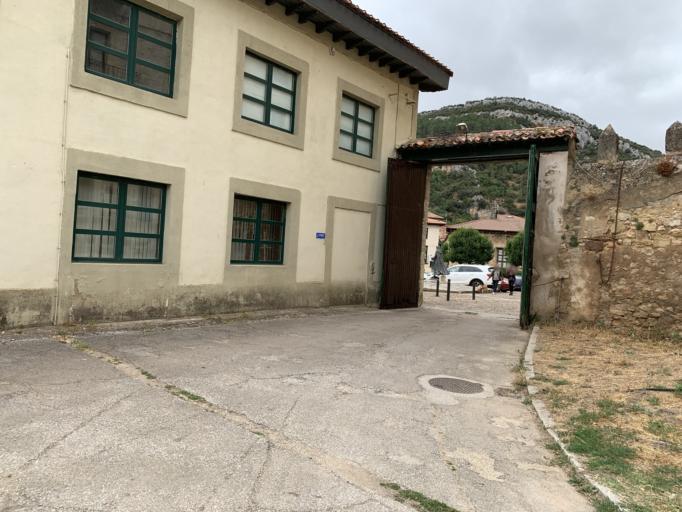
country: ES
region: Castille and Leon
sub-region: Provincia de Burgos
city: Ona
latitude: 42.7336
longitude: -3.4139
